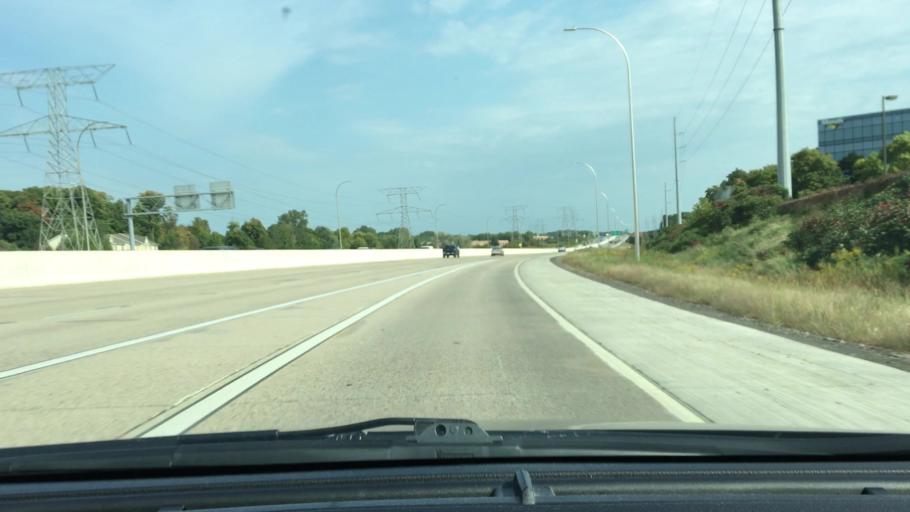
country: US
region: Minnesota
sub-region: Hennepin County
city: Plymouth
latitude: 45.0140
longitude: -93.4570
